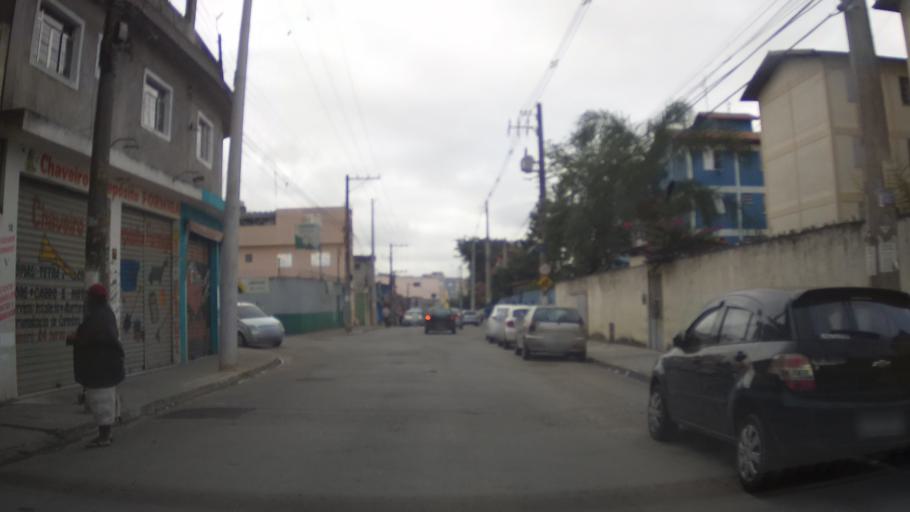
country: BR
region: Sao Paulo
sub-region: Itaquaquecetuba
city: Itaquaquecetuba
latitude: -23.4523
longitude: -46.4018
